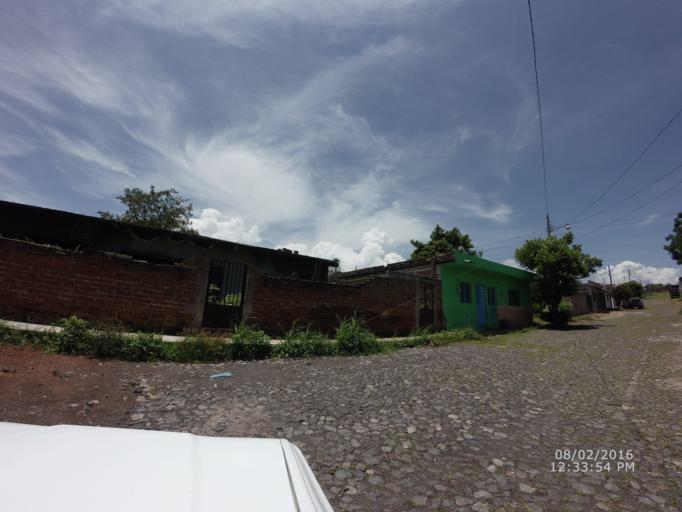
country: MX
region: Nayarit
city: Ixtlan del Rio
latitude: 21.0312
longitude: -104.3507
